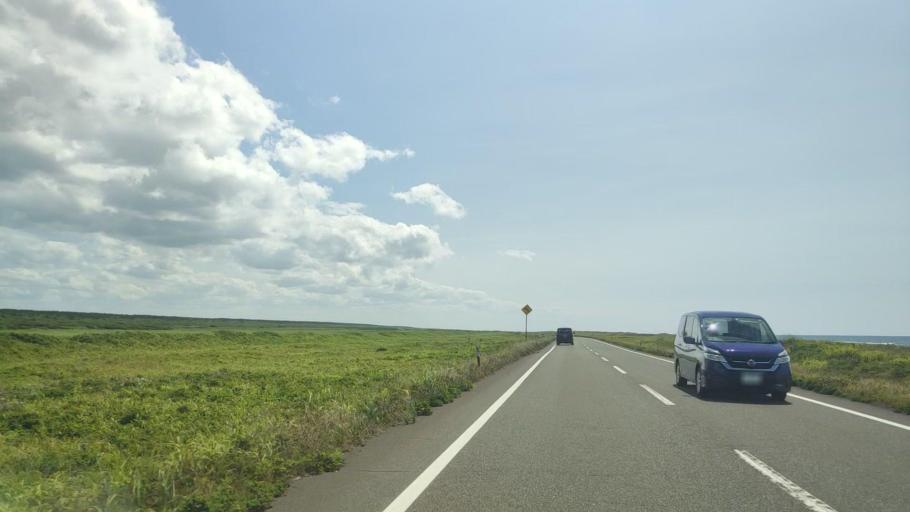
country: JP
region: Hokkaido
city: Wakkanai
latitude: 45.1638
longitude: 141.5845
